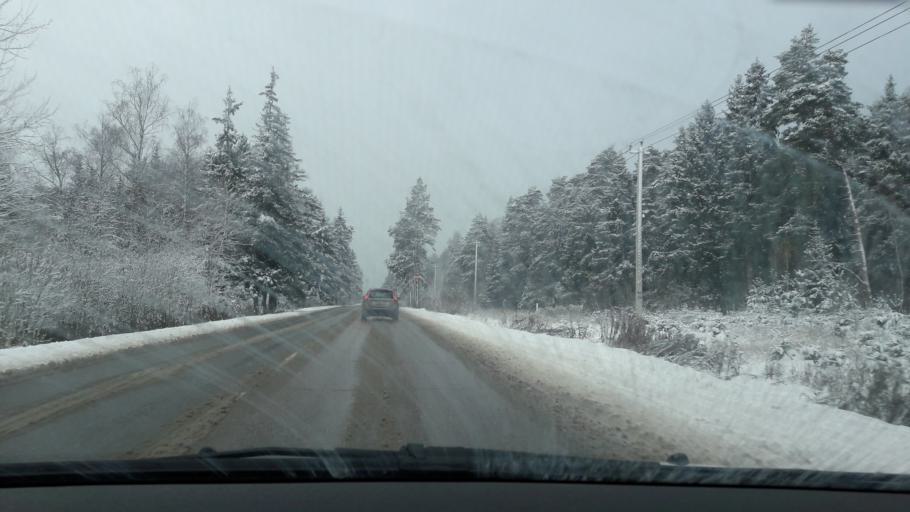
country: RU
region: Moskovskaya
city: Zvenigorod
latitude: 55.6385
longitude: 36.8474
